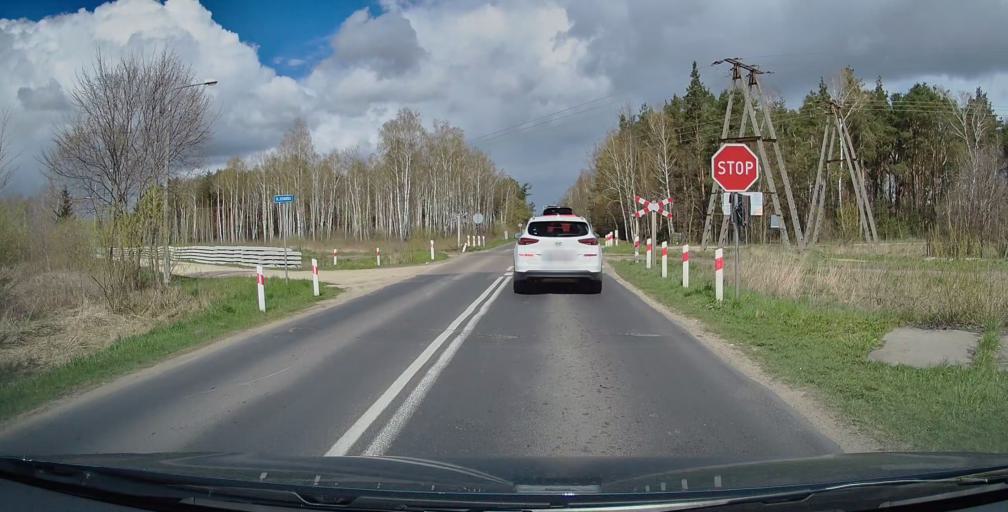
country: PL
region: Masovian Voivodeship
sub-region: Ostroleka
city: Ostroleka
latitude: 53.0562
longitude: 21.5860
